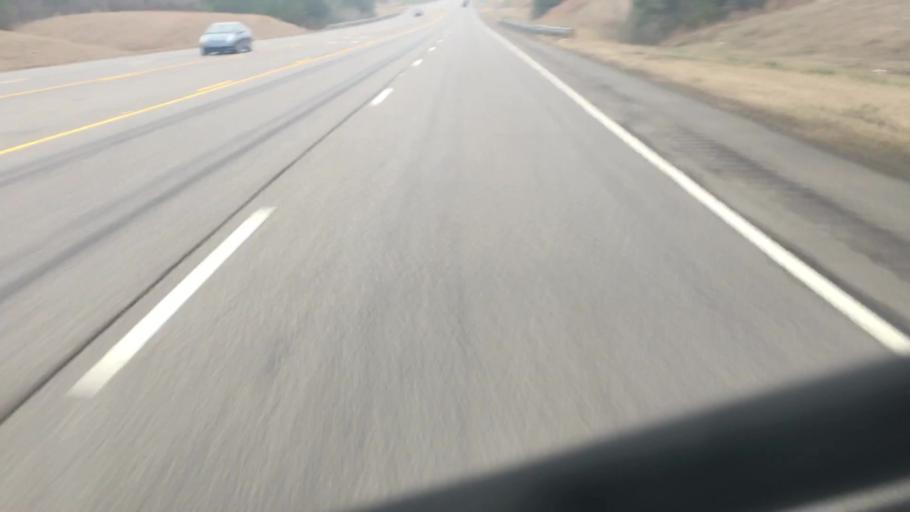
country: US
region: Alabama
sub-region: Walker County
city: Jasper
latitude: 33.8040
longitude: -87.2353
